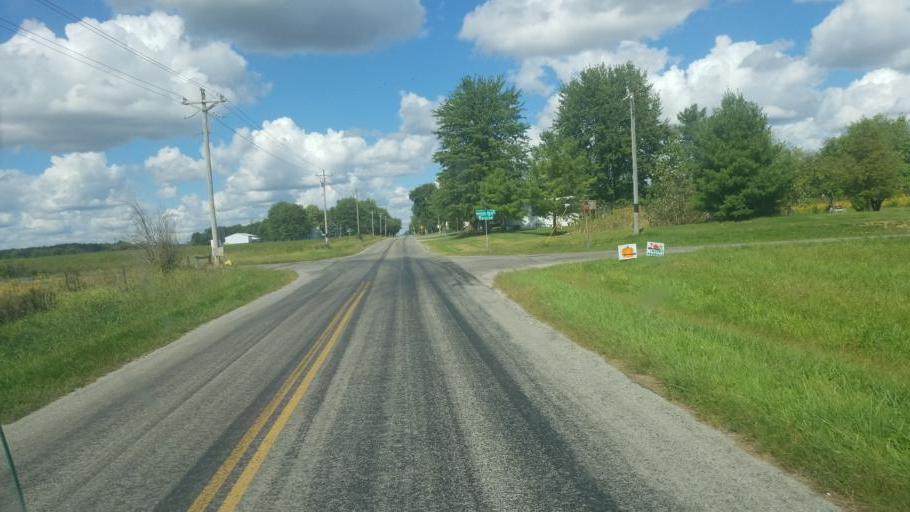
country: US
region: Ohio
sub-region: Champaign County
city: North Lewisburg
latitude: 40.3644
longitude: -83.5116
